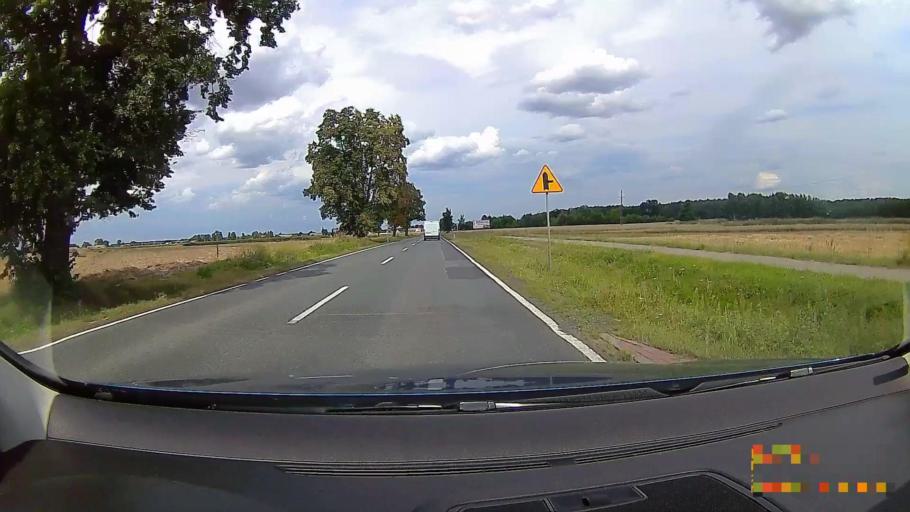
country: PL
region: Greater Poland Voivodeship
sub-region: Powiat koninski
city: Rychwal
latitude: 52.0861
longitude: 18.1631
